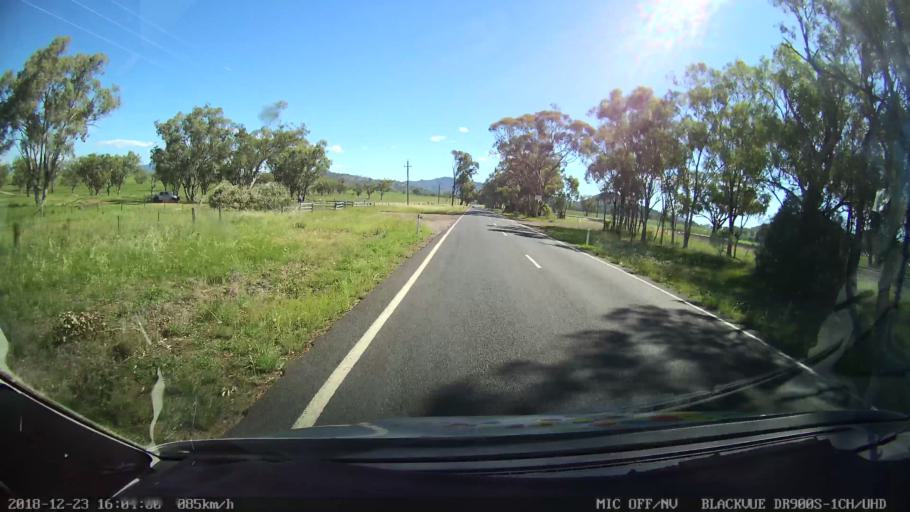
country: AU
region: New South Wales
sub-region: Tamworth Municipality
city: Phillip
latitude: -31.2500
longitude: 150.7959
